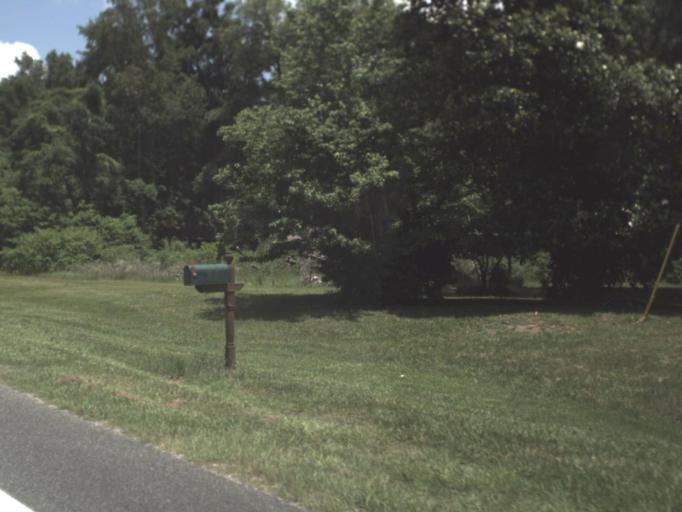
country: US
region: Florida
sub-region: Alachua County
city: High Springs
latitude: 29.8948
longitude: -82.6794
